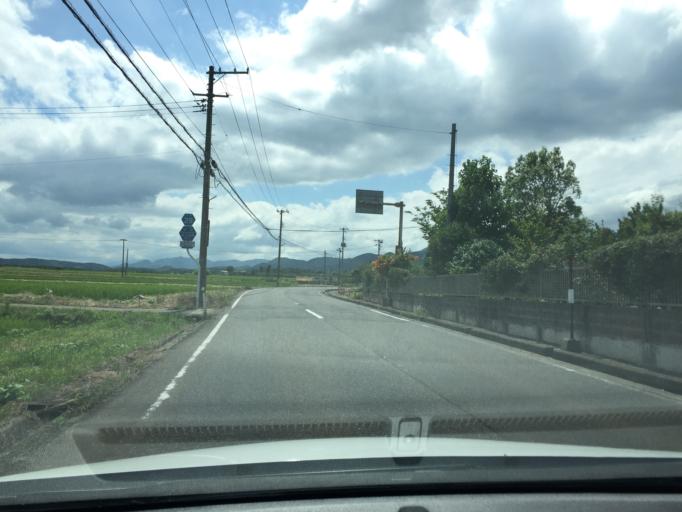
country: JP
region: Fukushima
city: Koriyama
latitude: 37.3461
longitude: 140.2637
